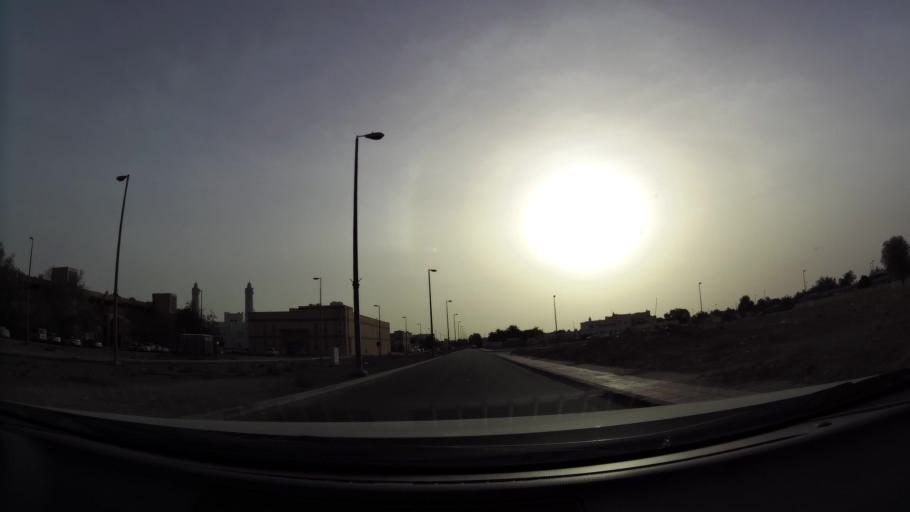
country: OM
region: Al Buraimi
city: Al Buraymi
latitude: 24.2427
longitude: 55.7464
